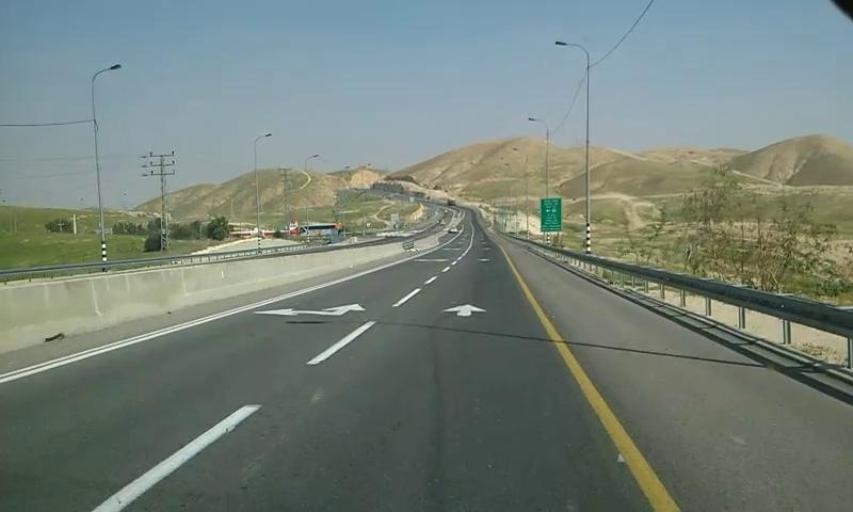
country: PS
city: Az Za`ayyim
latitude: 31.8141
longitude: 35.3485
